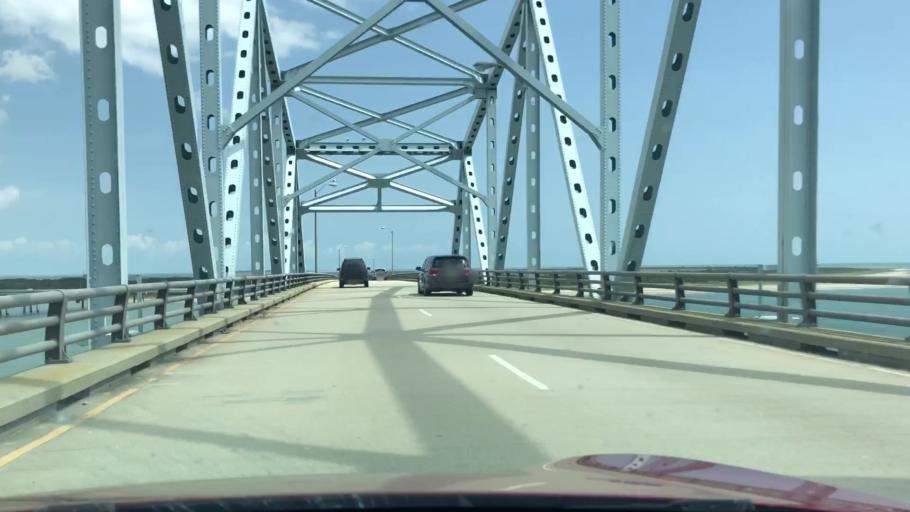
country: US
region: Virginia
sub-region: Northampton County
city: Cape Charles
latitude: 37.0886
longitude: -75.9874
